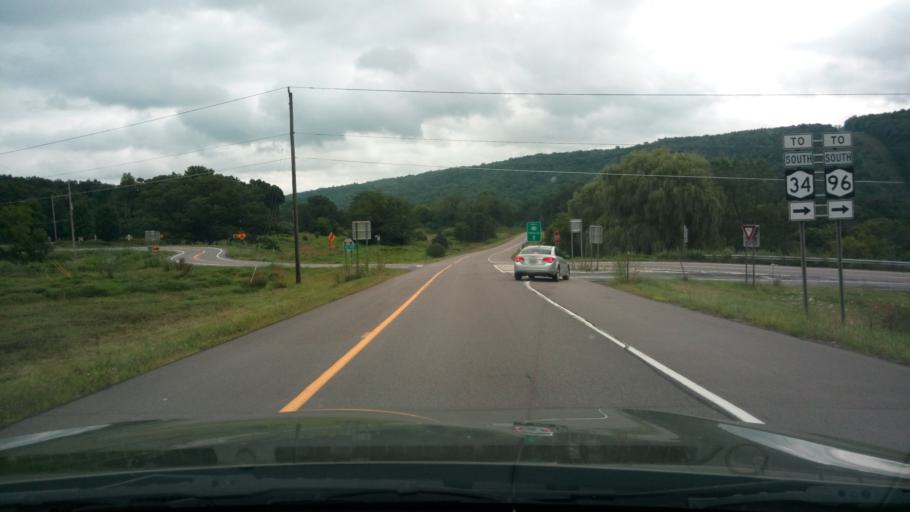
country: US
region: New York
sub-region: Tompkins County
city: South Hill
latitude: 42.3920
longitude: -76.5549
